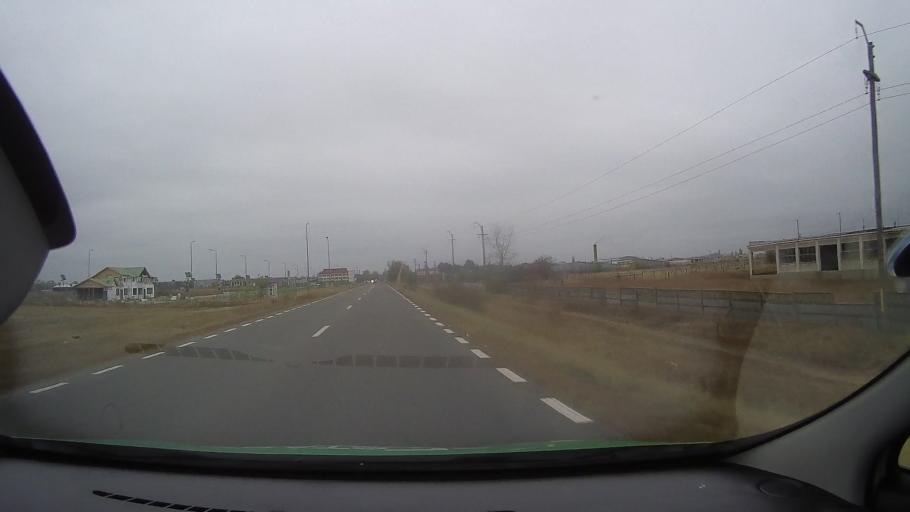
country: RO
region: Ialomita
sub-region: Comuna Slobozia
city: Slobozia
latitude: 44.5833
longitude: 27.3884
